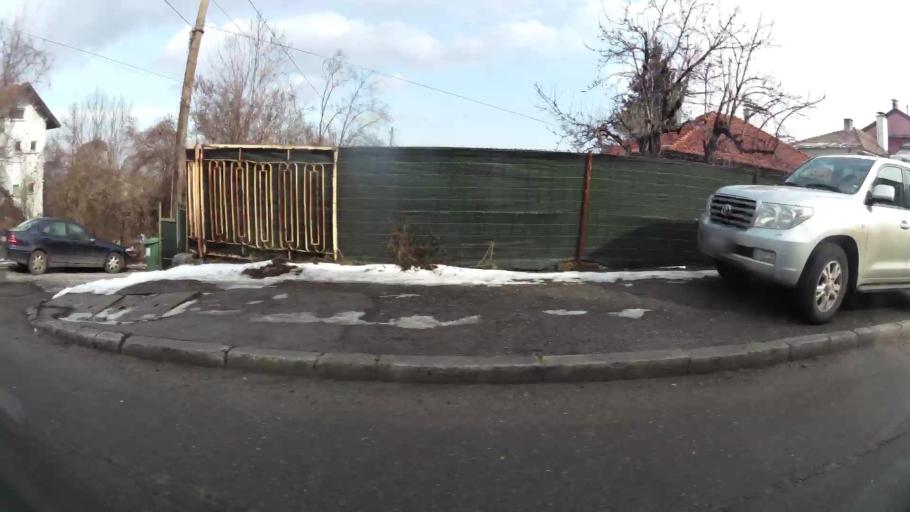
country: BG
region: Sofia-Capital
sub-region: Stolichna Obshtina
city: Sofia
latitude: 42.6481
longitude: 23.2647
